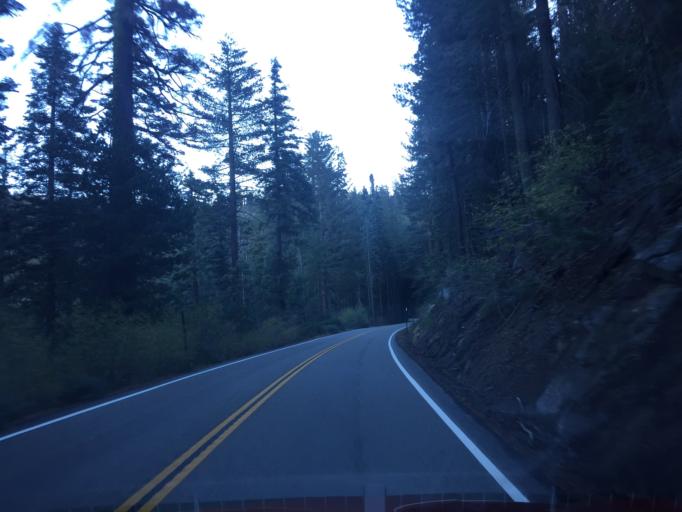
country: US
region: California
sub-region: Mariposa County
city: Yosemite Valley
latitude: 37.6650
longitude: -119.7025
